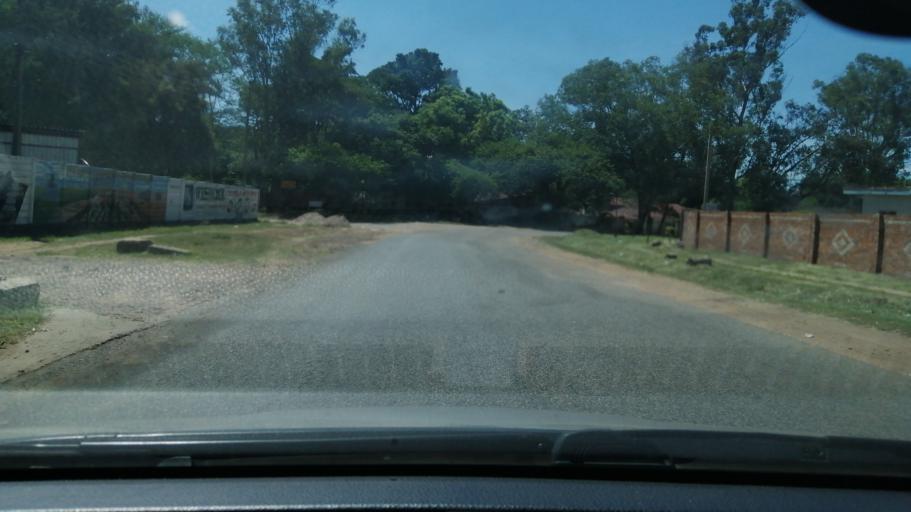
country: ZW
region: Harare
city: Epworth
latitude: -17.8413
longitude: 31.1206
